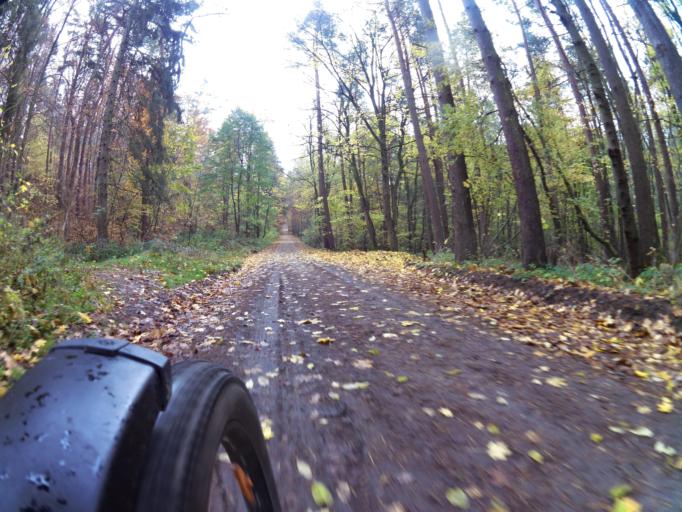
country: PL
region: Pomeranian Voivodeship
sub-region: Powiat pucki
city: Krokowa
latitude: 54.7817
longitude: 18.0889
